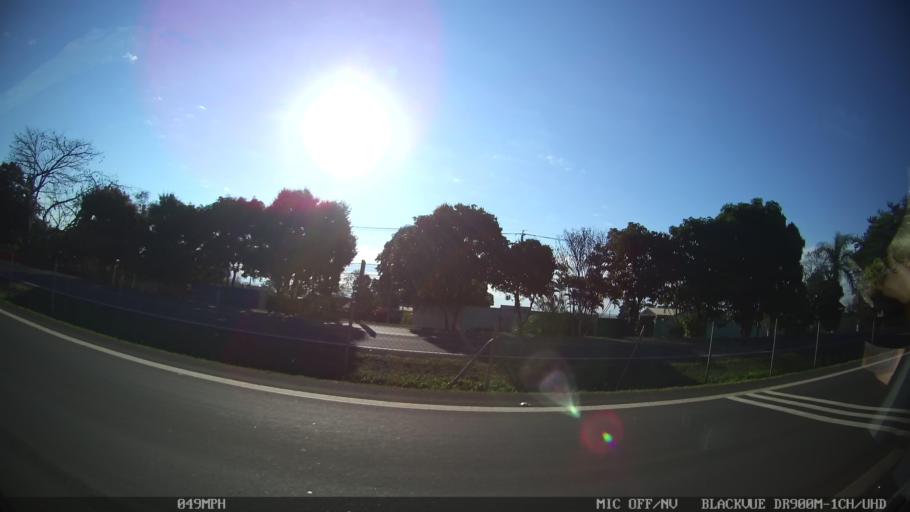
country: BR
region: Sao Paulo
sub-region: Piracicaba
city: Piracicaba
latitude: -22.6696
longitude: -47.6254
